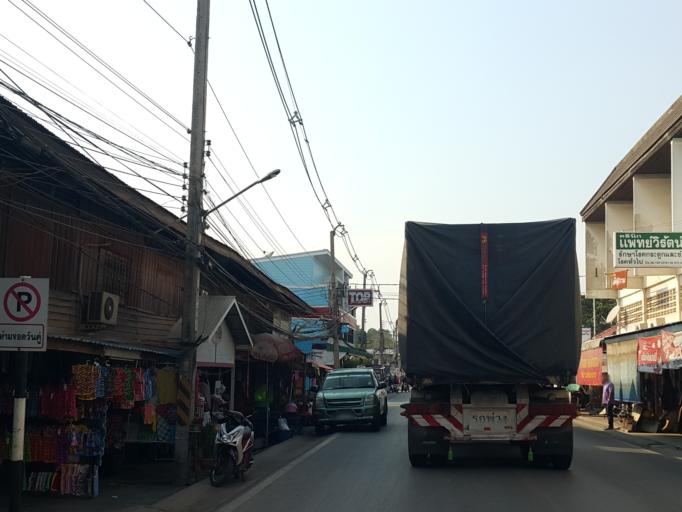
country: TH
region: Phitsanulok
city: Phrom Phiram
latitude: 17.0344
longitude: 100.1993
